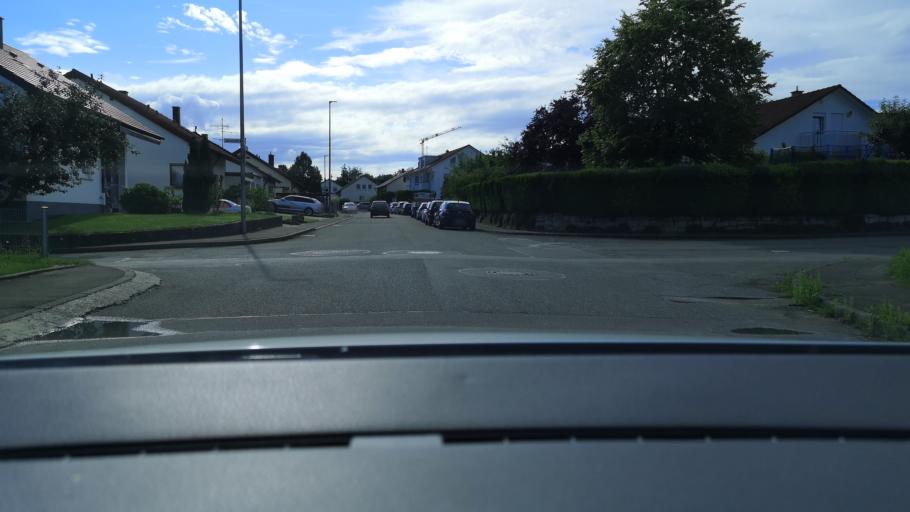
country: DE
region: Baden-Wuerttemberg
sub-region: Tuebingen Region
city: Pliezhausen
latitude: 48.5915
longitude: 9.1757
